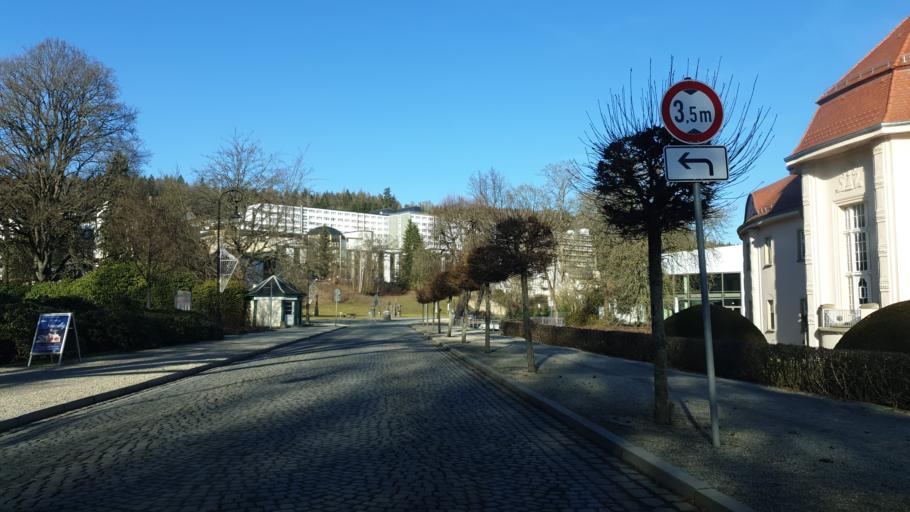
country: DE
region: Saxony
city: Bad Elster
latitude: 50.2831
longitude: 12.2388
